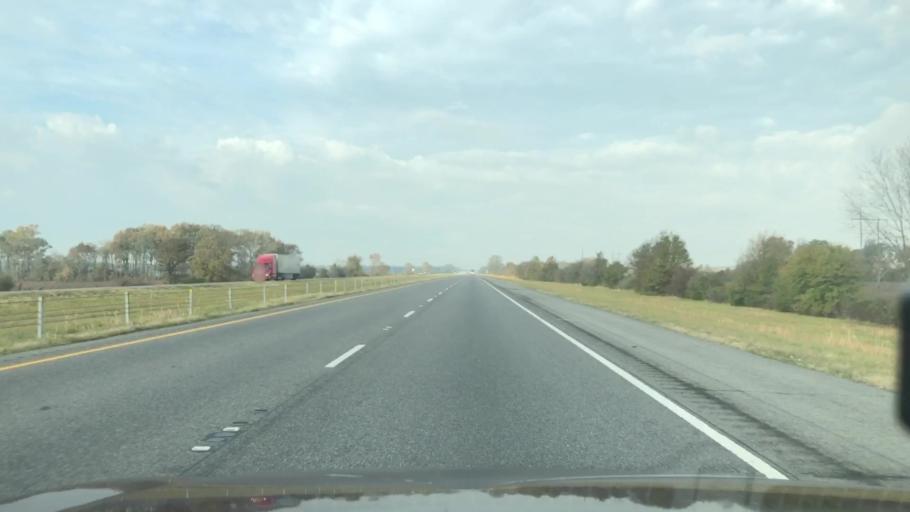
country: US
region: Louisiana
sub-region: Madison Parish
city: Tallulah
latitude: 32.4217
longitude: -91.3301
